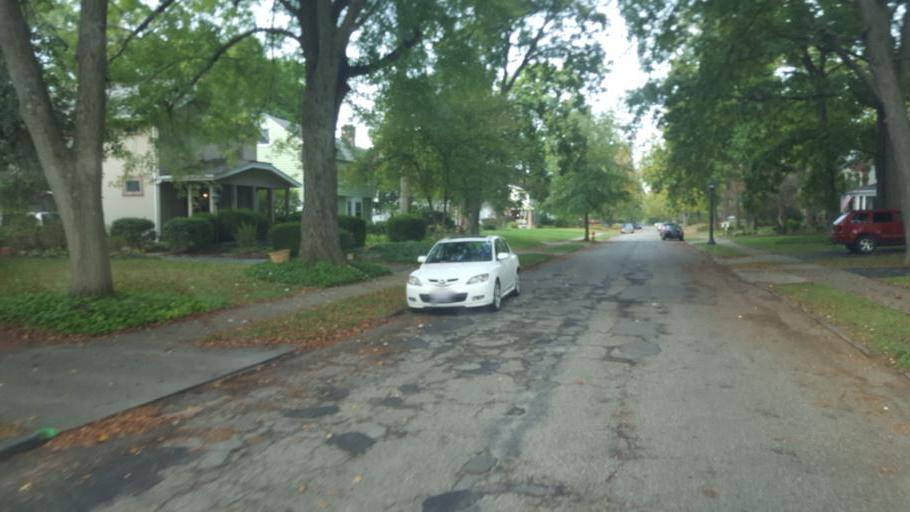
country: US
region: Ohio
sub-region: Franklin County
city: Worthington
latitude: 40.0360
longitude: -83.0021
